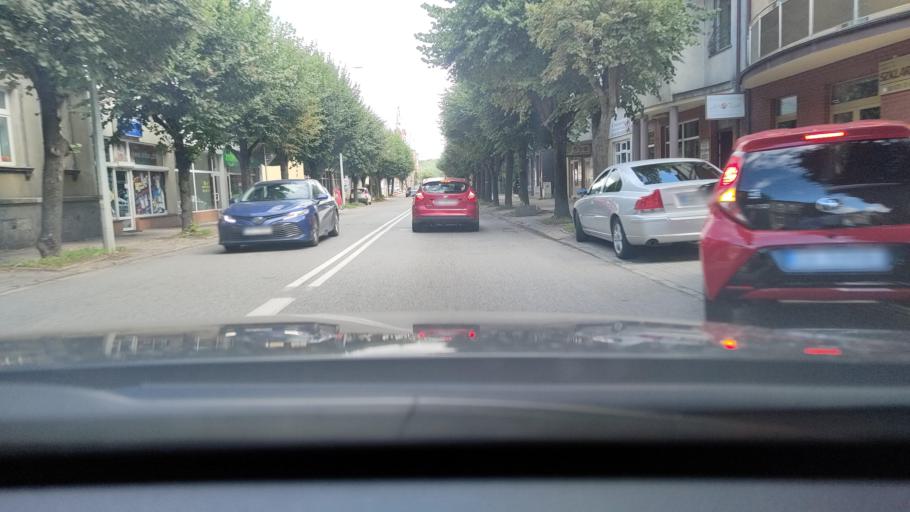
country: PL
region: Pomeranian Voivodeship
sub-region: Powiat wejherowski
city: Wejherowo
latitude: 54.5994
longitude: 18.2326
